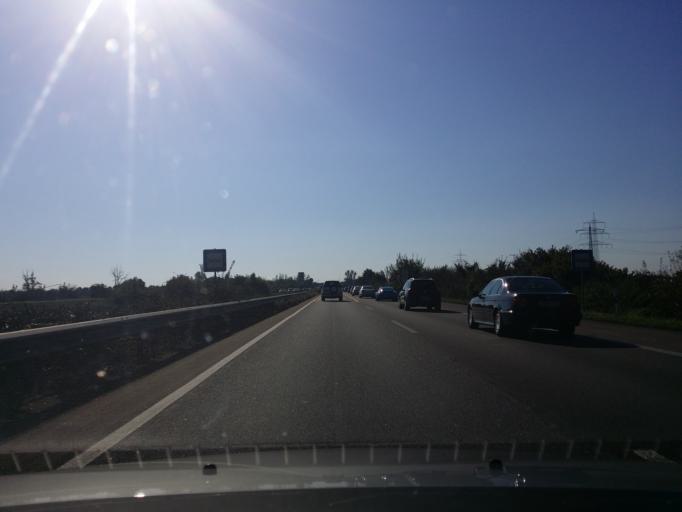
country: DE
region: Rheinland-Pfalz
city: Maxdorf
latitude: 49.4909
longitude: 8.3119
